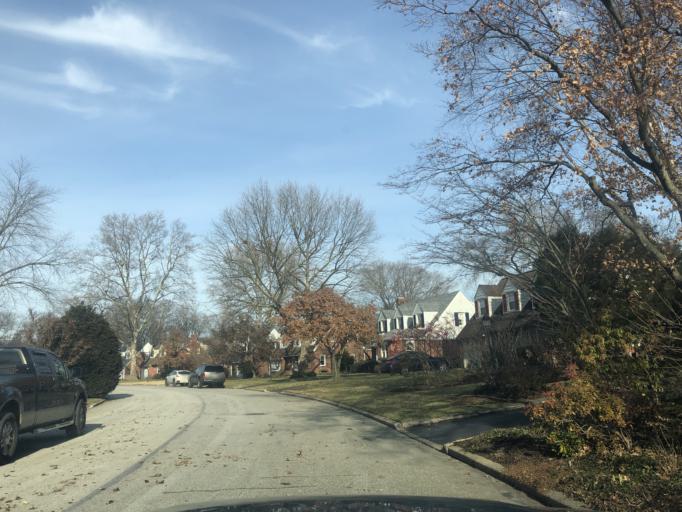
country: US
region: Pennsylvania
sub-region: Montgomery County
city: Oreland
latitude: 40.1146
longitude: -75.1940
